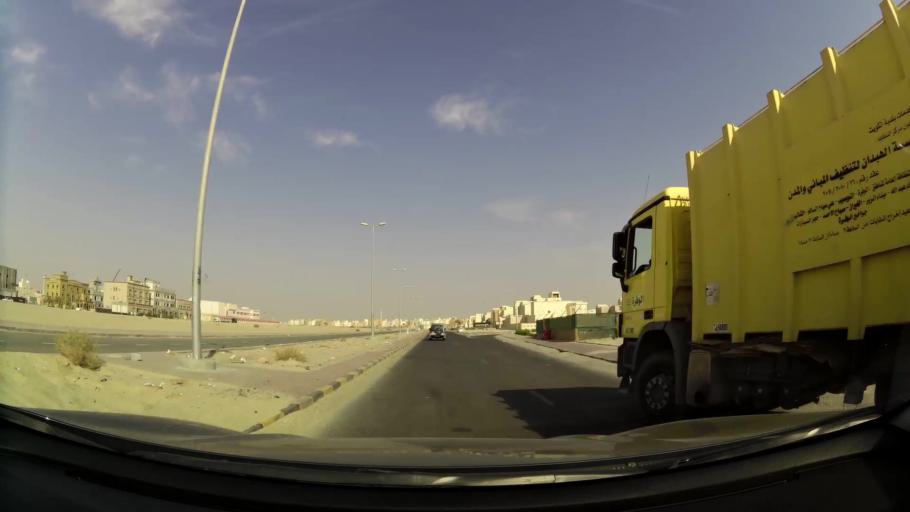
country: KW
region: Al Ahmadi
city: Al Wafrah
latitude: 28.7912
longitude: 48.0670
